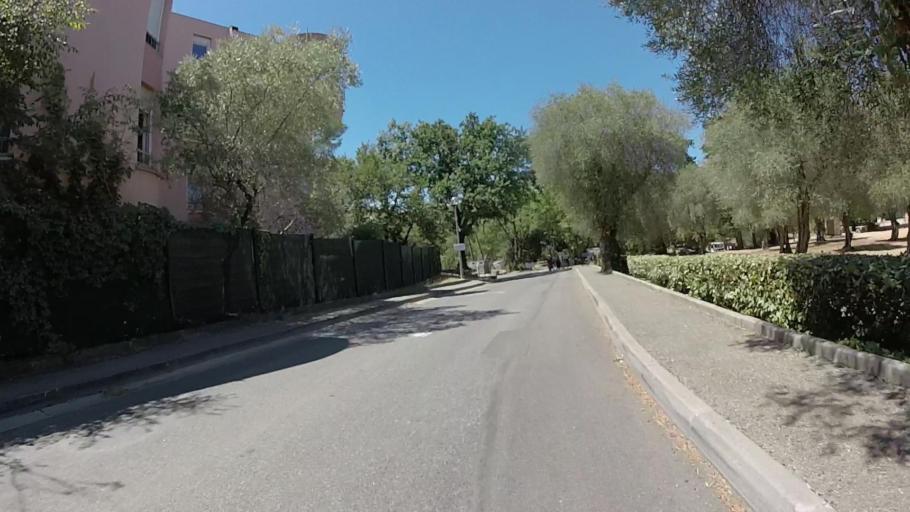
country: FR
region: Provence-Alpes-Cote d'Azur
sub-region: Departement des Alpes-Maritimes
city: Vallauris
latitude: 43.6224
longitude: 7.0448
